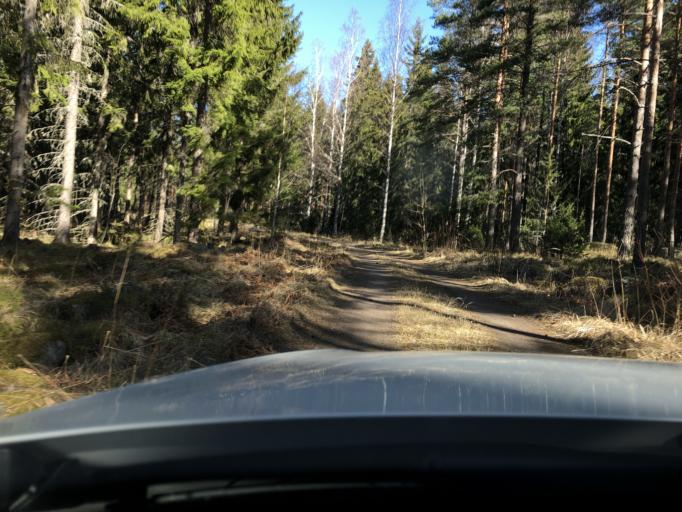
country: SE
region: Uppsala
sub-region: Heby Kommun
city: OEstervala
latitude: 60.3263
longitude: 17.1744
